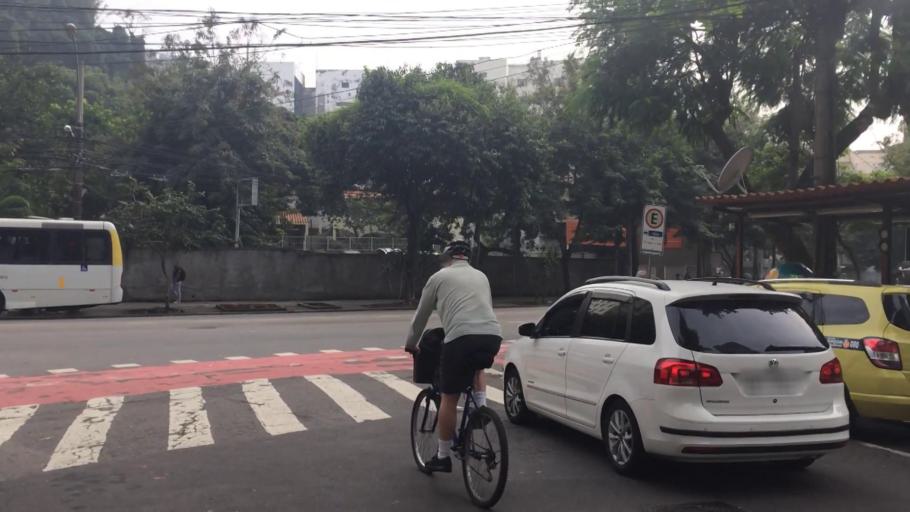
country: BR
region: Rio de Janeiro
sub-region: Rio De Janeiro
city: Rio de Janeiro
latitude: -22.9383
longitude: -43.1909
